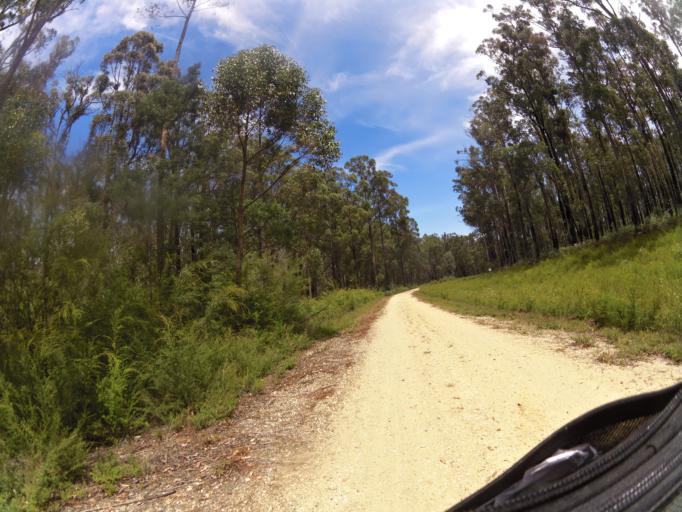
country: AU
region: Victoria
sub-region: East Gippsland
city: Lakes Entrance
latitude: -37.7447
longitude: 148.0381
